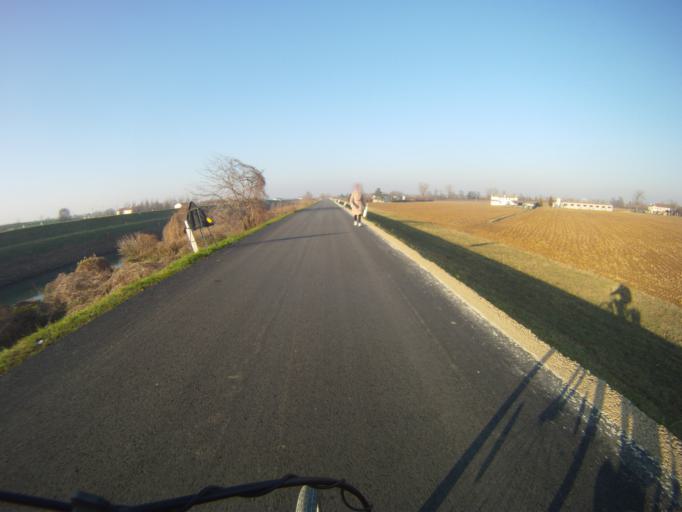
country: IT
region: Veneto
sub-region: Provincia di Padova
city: Polverara
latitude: 45.3256
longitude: 11.9408
